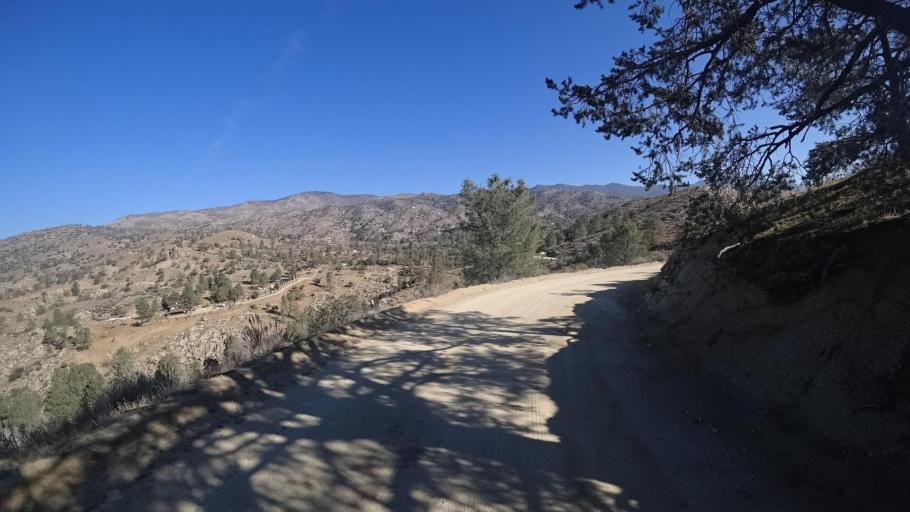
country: US
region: California
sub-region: Kern County
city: Bodfish
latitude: 35.3839
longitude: -118.4112
